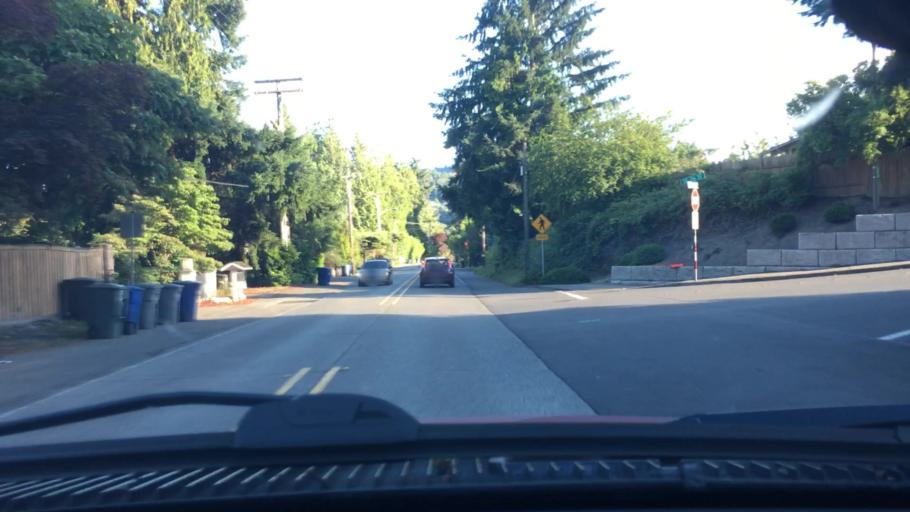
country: US
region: Washington
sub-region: King County
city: West Lake Sammamish
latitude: 47.5864
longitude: -122.1115
